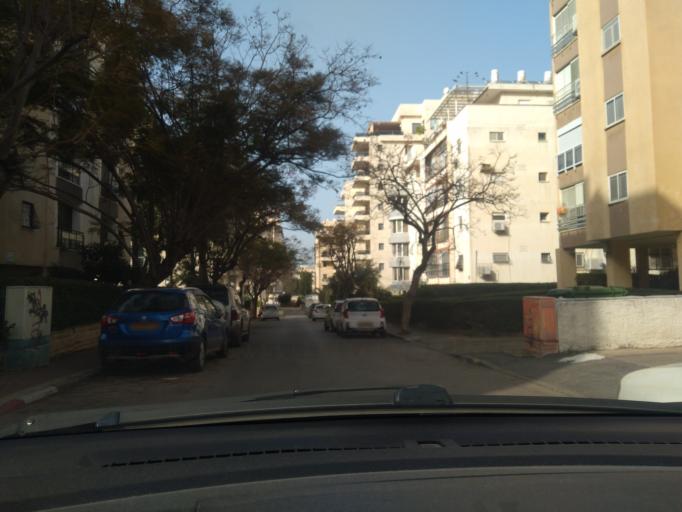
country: IL
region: Central District
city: Netanya
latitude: 32.3362
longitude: 34.8583
